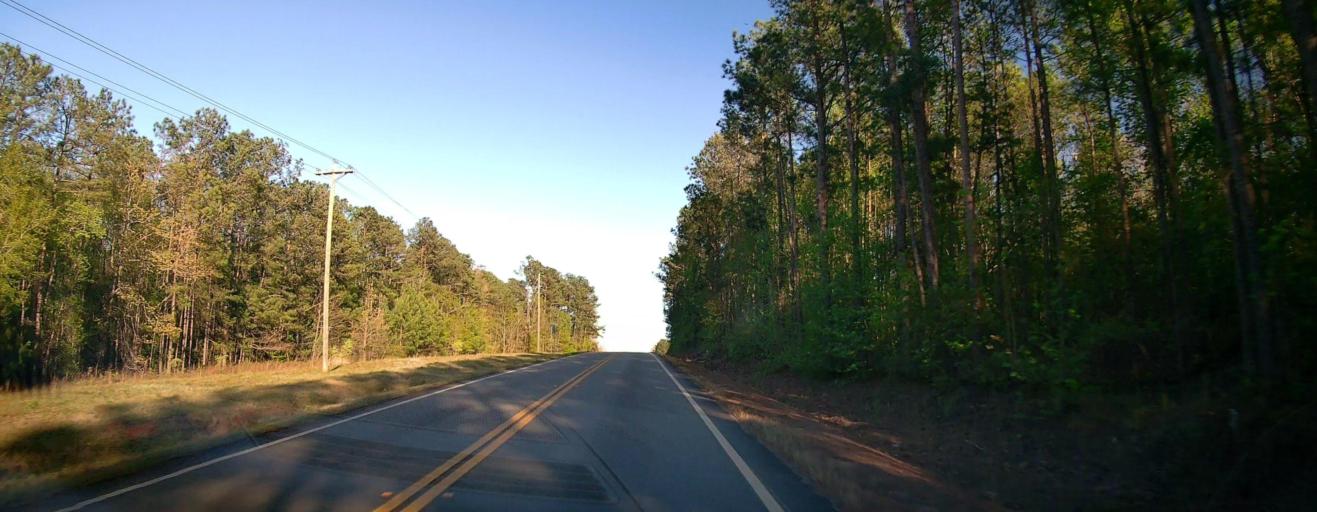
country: US
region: Georgia
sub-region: Wilkinson County
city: Irwinton
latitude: 32.8580
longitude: -83.0752
